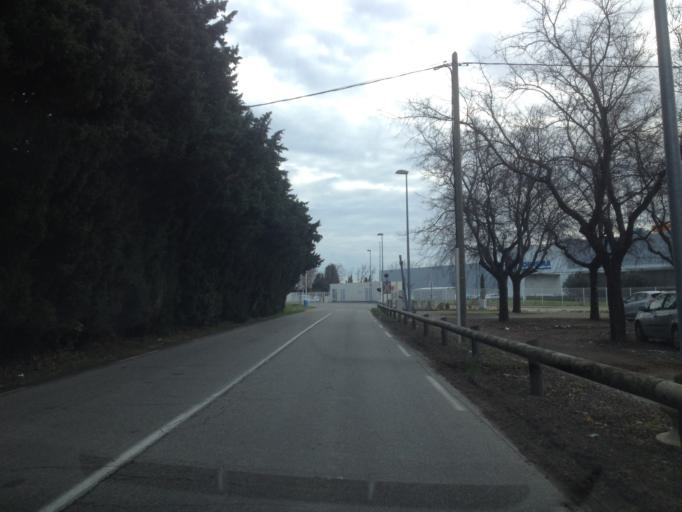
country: FR
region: Provence-Alpes-Cote d'Azur
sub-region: Departement du Vaucluse
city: Sorgues
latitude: 43.9922
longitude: 4.8650
